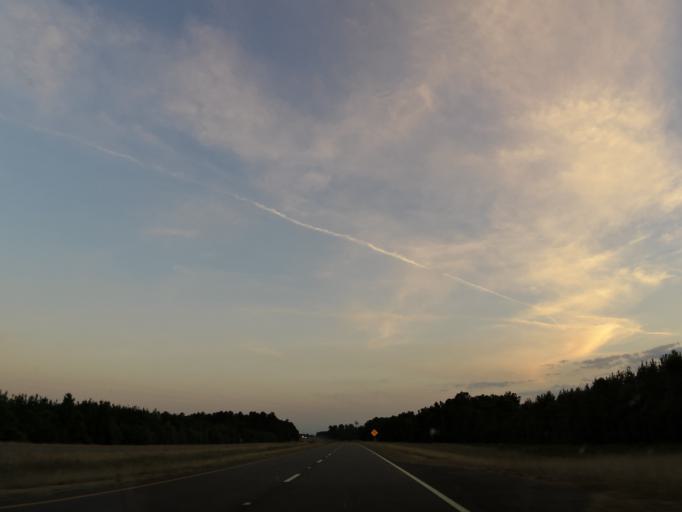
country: US
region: Mississippi
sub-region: Kemper County
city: De Kalb
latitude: 32.7619
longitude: -88.4653
